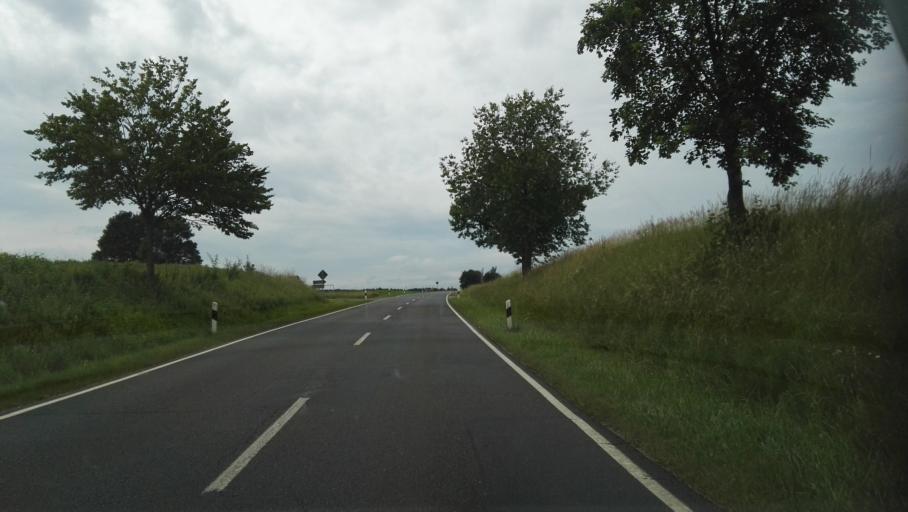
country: DE
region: Bavaria
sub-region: Upper Franconia
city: Plankenfels
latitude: 49.9120
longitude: 11.3164
